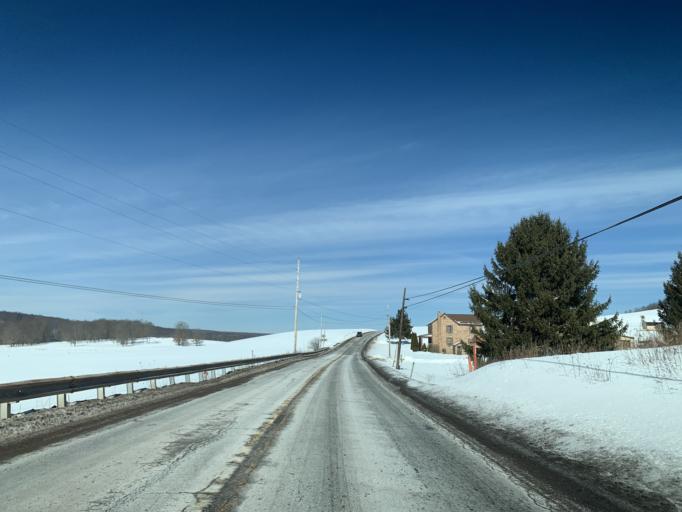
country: US
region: West Virginia
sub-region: Preston County
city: Terra Alta
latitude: 39.7115
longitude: -79.4455
